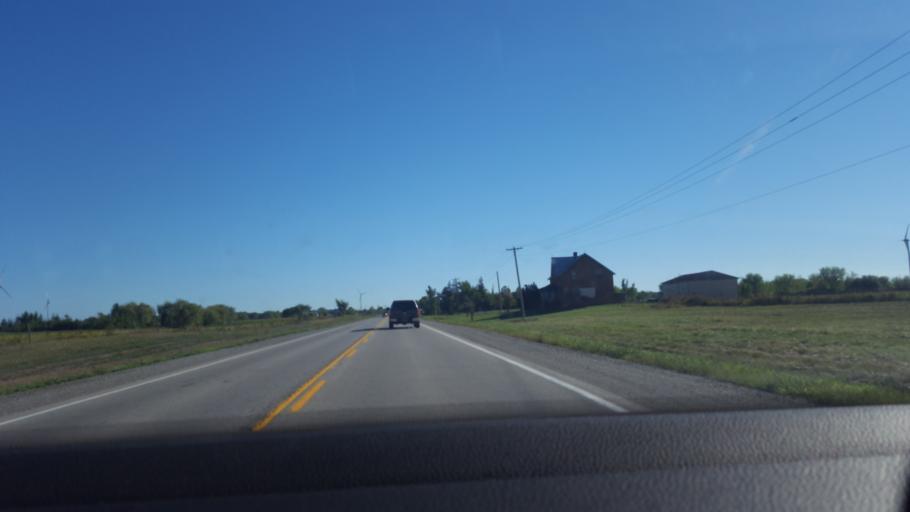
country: CA
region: Ontario
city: Welland
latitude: 43.0504
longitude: -79.5034
